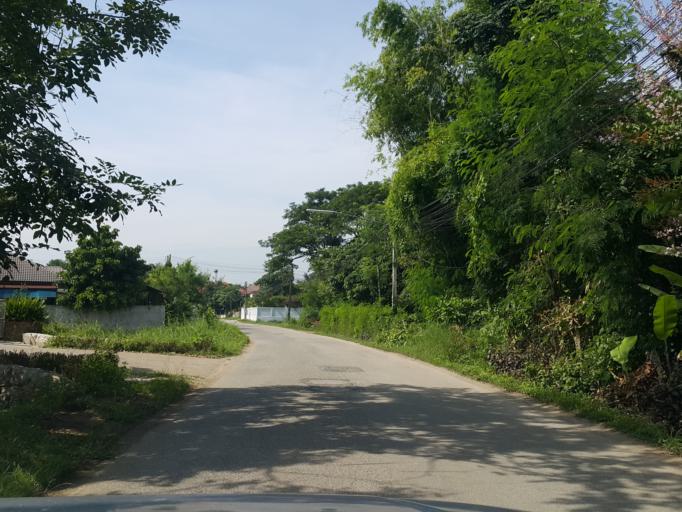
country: TH
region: Chiang Mai
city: San Kamphaeng
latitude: 18.7240
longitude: 99.0980
